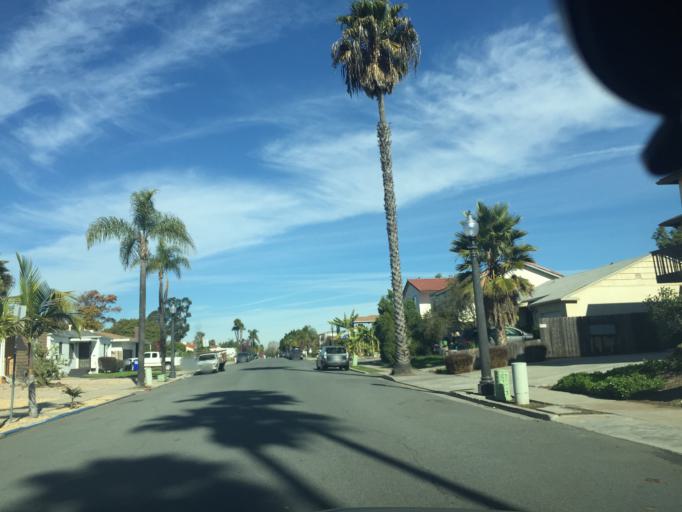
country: US
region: California
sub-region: San Diego County
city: Lemon Grove
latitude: 32.7602
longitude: -117.0878
